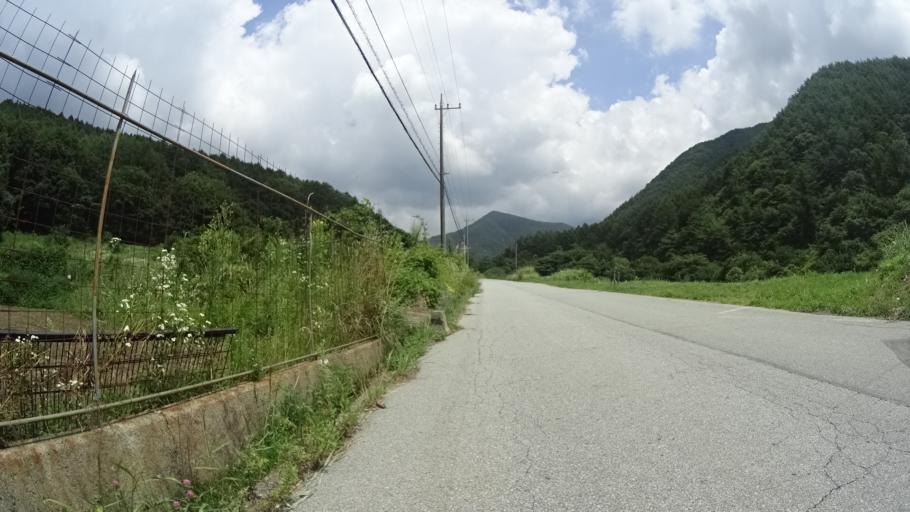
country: JP
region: Yamanashi
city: Nirasaki
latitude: 35.8907
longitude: 138.5338
